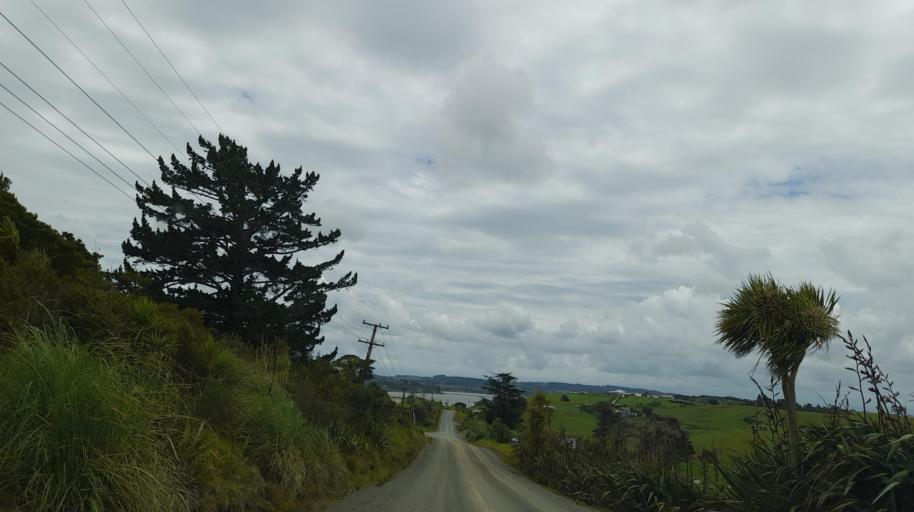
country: NZ
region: Auckland
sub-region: Auckland
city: Wellsford
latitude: -36.2690
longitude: 174.4084
